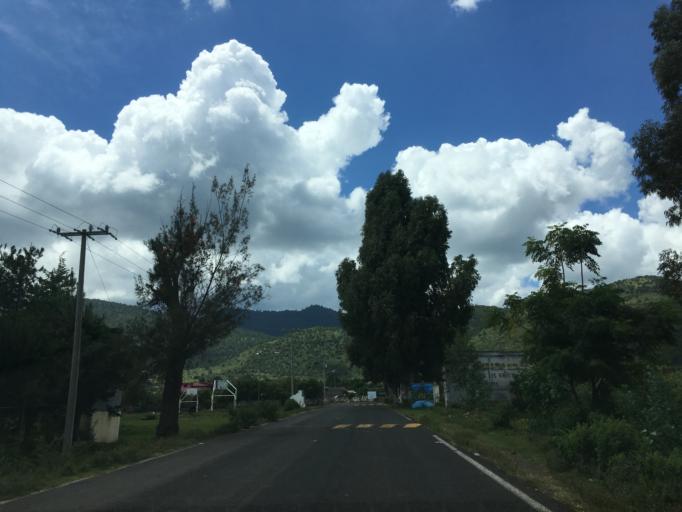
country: MX
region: Mexico
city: Huaniqueo de Morales
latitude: 19.7907
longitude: -101.4685
